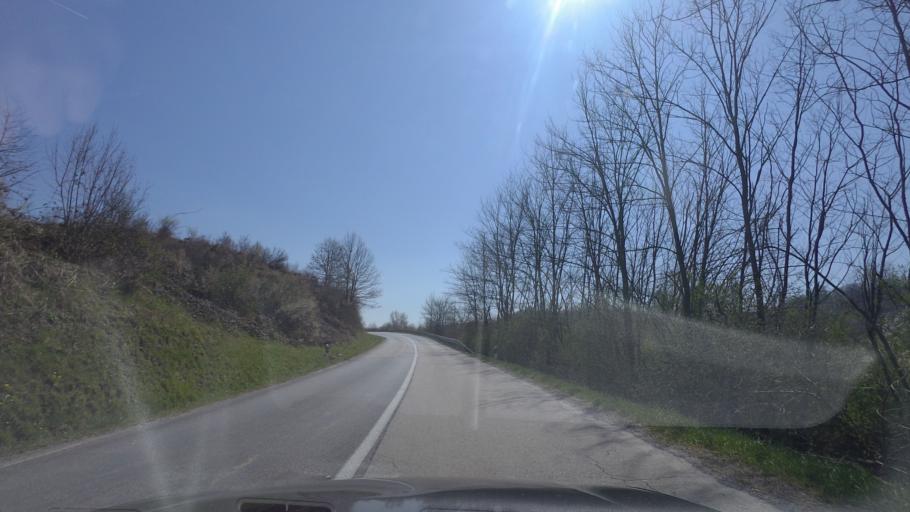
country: HR
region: Karlovacka
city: Vojnic
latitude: 45.3500
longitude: 15.6765
